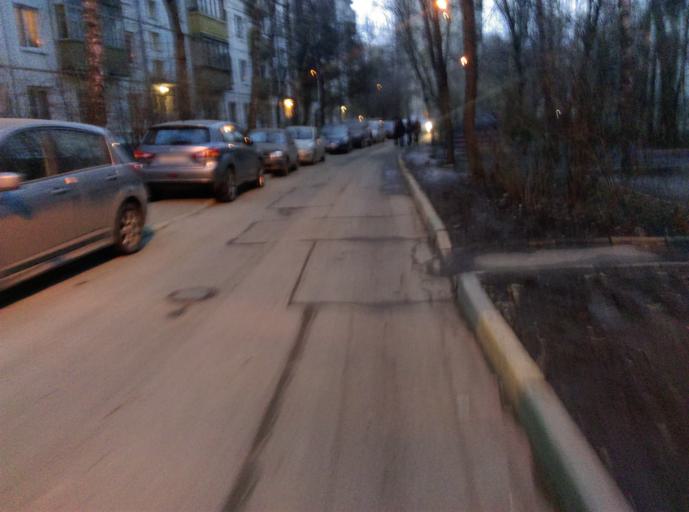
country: RU
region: Moskovskaya
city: Vostryakovo
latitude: 55.6734
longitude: 37.4470
